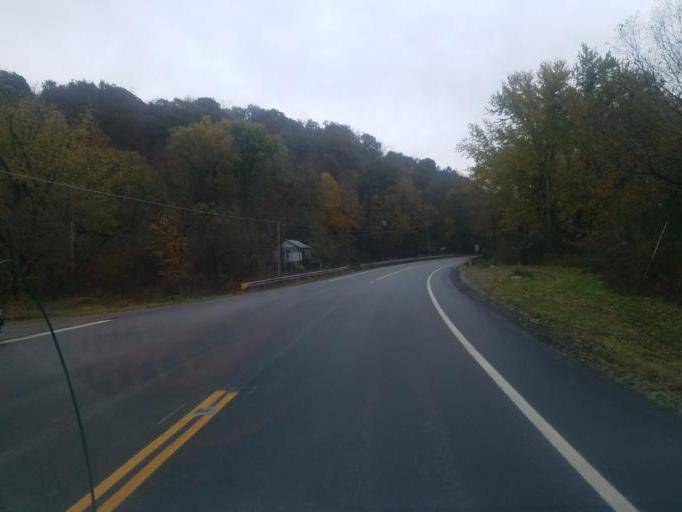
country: US
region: Ohio
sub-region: Washington County
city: Beverly
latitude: 39.5670
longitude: -81.5796
